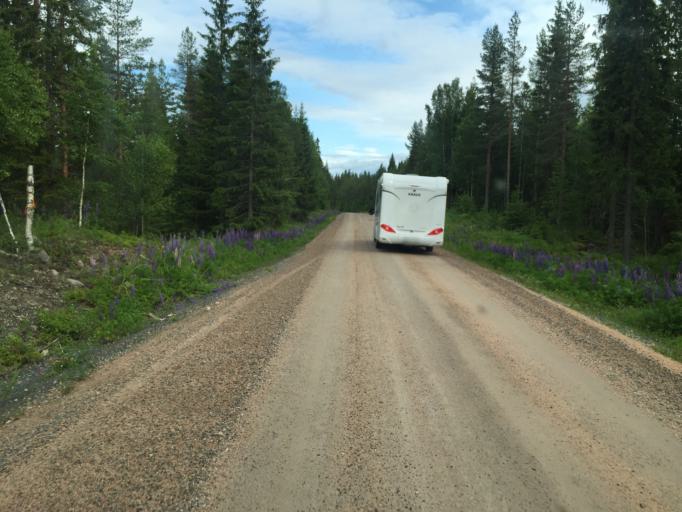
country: SE
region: Dalarna
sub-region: Malung-Saelens kommun
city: Malung
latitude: 60.8938
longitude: 13.6702
